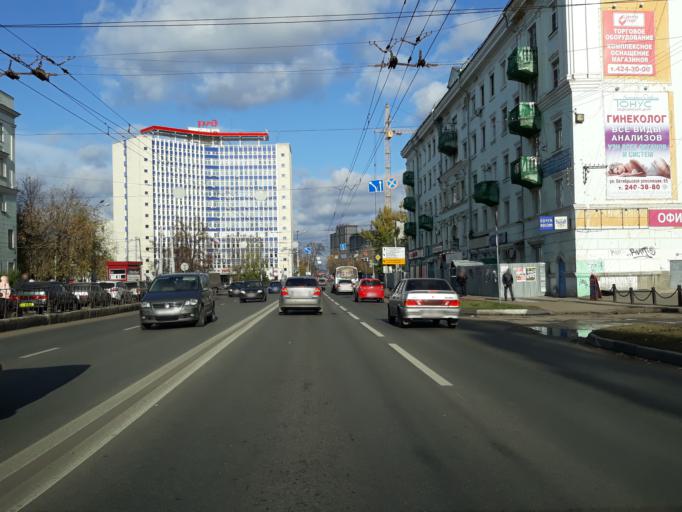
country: RU
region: Nizjnij Novgorod
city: Nizhniy Novgorod
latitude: 56.3000
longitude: 43.9389
